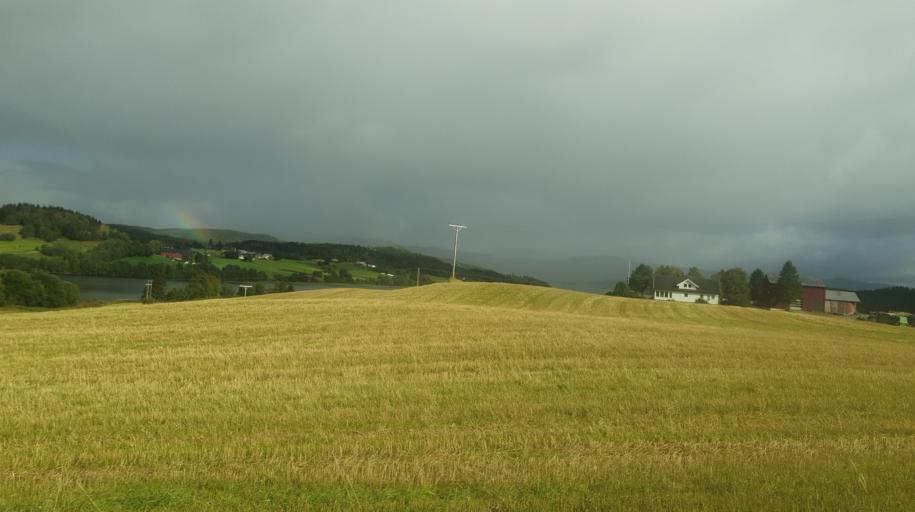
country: NO
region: Nord-Trondelag
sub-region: Levanger
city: Skogn
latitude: 63.6203
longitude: 11.1640
